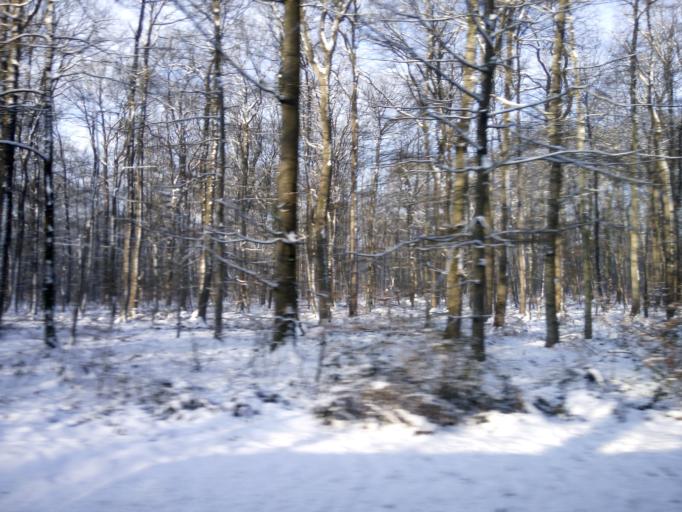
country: LU
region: Grevenmacher
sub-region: Canton d'Echternach
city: Berdorf
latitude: 49.8091
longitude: 6.3405
